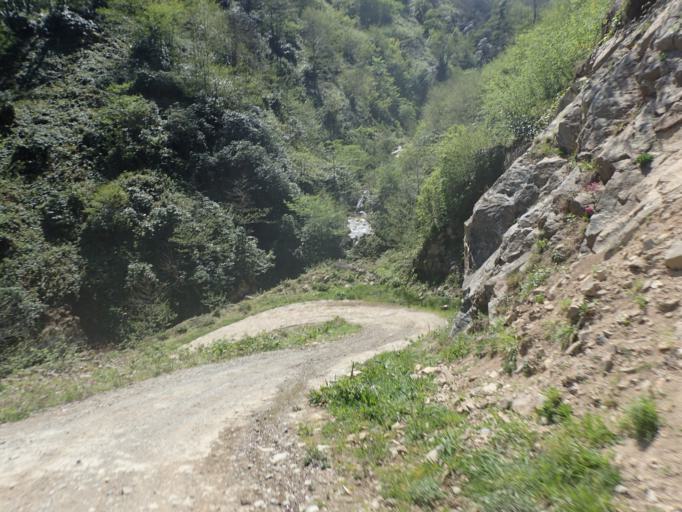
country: TR
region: Ordu
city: Kabaduz
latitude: 40.7372
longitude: 37.8920
